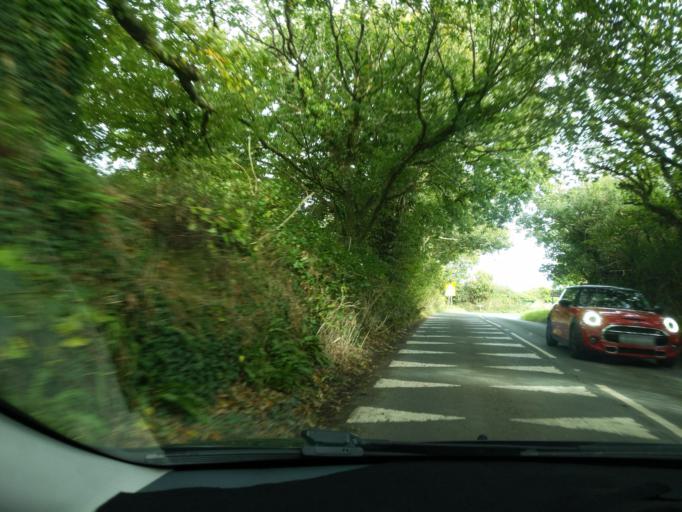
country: GB
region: England
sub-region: Cornwall
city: Mevagissey
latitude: 50.2472
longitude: -4.8113
